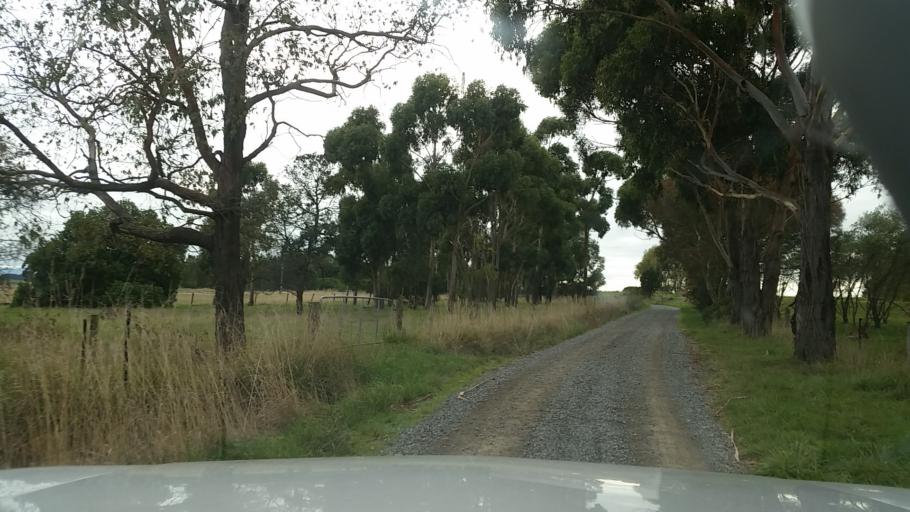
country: NZ
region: Marlborough
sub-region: Marlborough District
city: Blenheim
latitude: -41.5196
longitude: 174.0399
